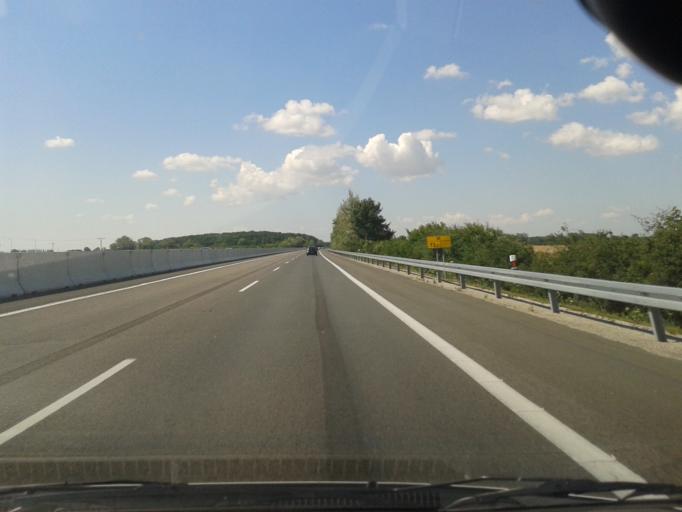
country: SK
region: Trnavsky
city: Leopoldov
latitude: 48.5045
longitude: 17.7662
